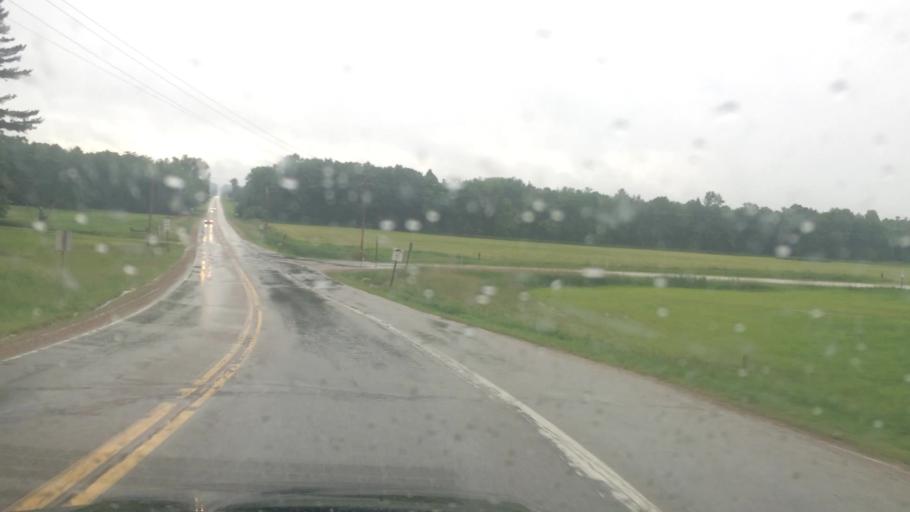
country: US
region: Wisconsin
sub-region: Waupaca County
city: Marion
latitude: 44.6094
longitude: -88.9003
